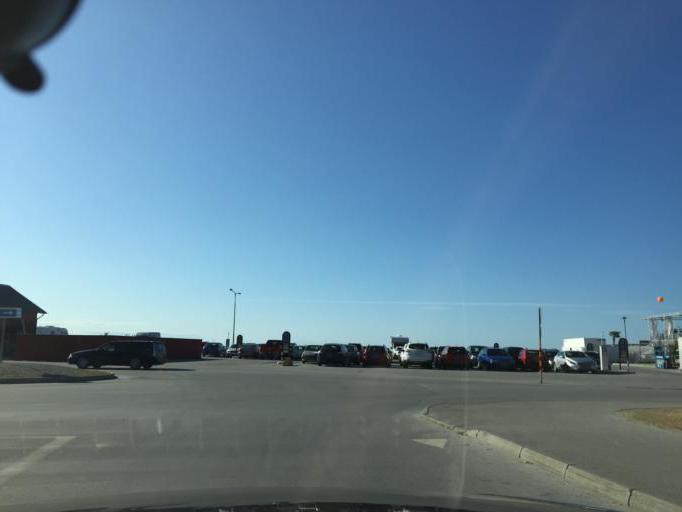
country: SE
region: Gotland
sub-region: Gotland
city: Visby
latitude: 57.6396
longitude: 18.2871
